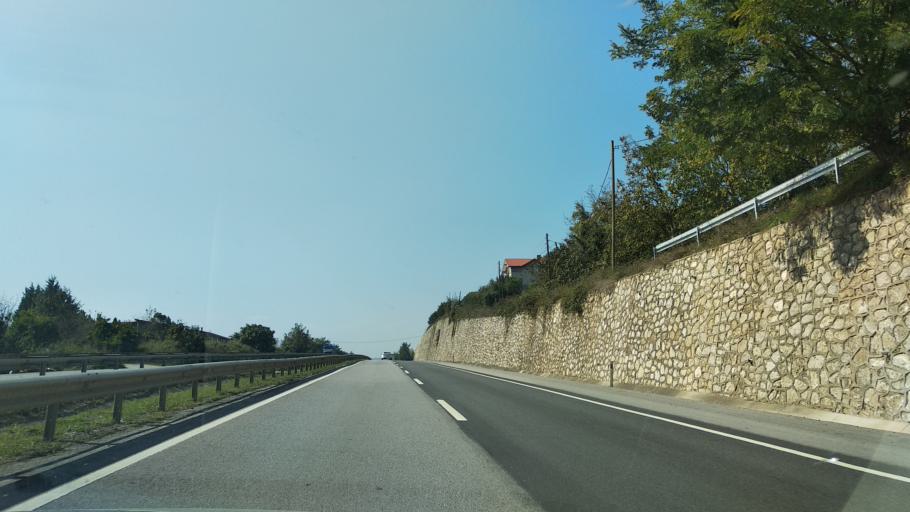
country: TR
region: Sakarya
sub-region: Merkez
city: Sapanca
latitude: 40.7354
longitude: 30.2369
